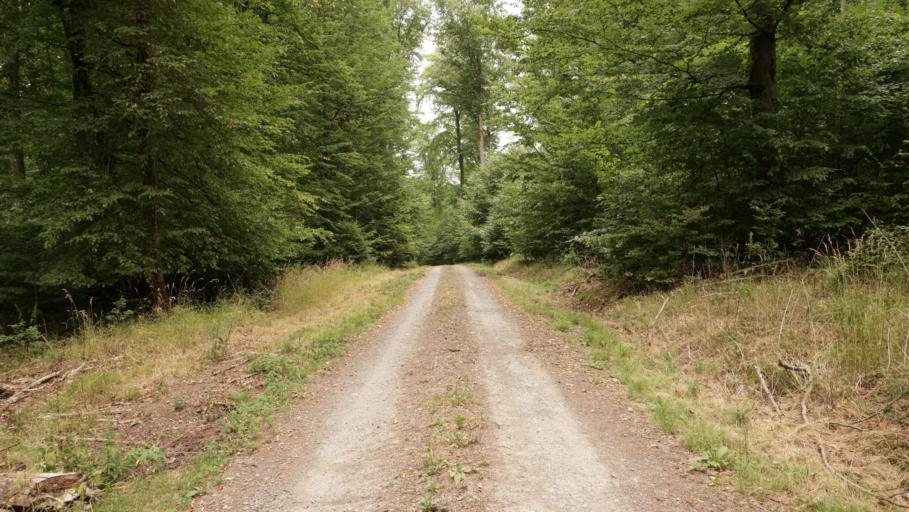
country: DE
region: Baden-Wuerttemberg
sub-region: Karlsruhe Region
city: Mosbach
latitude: 49.3885
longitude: 9.1542
